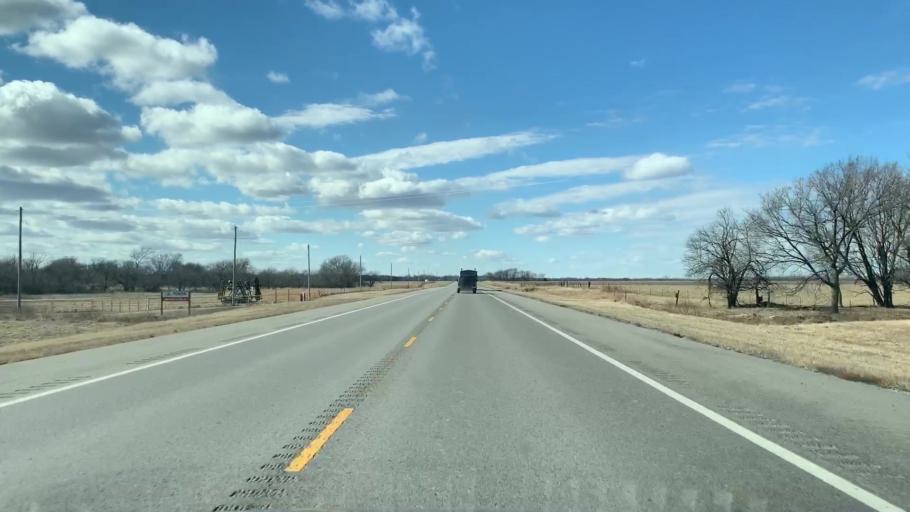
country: US
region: Kansas
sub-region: Crawford County
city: Pittsburg
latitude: 37.3397
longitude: -94.8588
